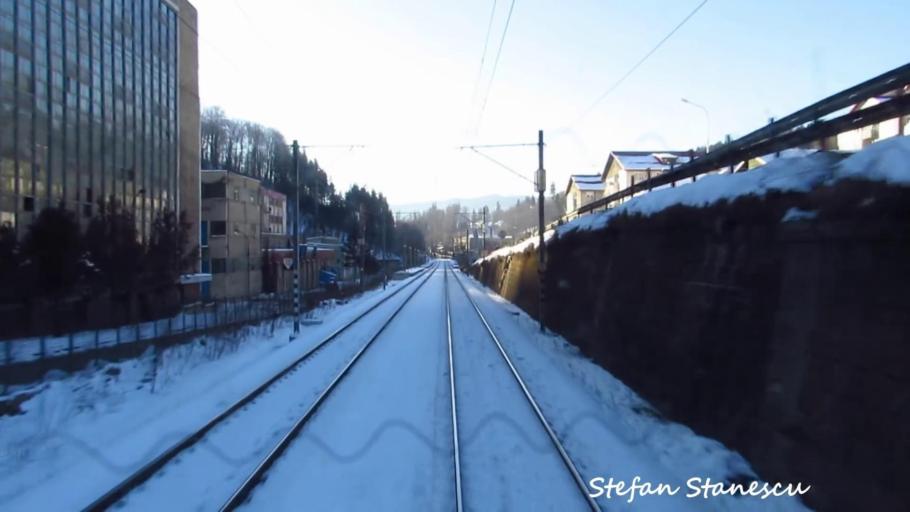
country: RO
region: Prahova
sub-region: Oras Sinaia
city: Sinaia
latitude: 45.3412
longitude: 25.5515
